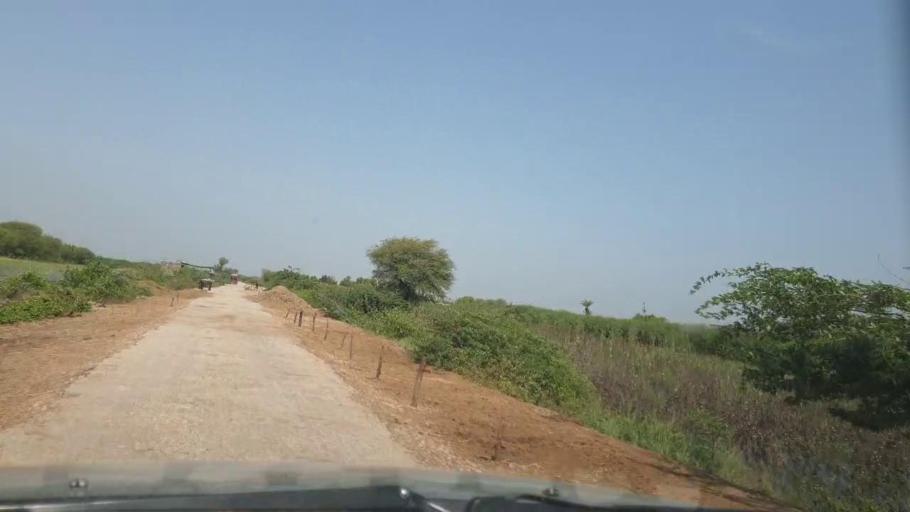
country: PK
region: Sindh
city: Tando Ghulam Ali
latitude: 25.0959
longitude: 68.8020
